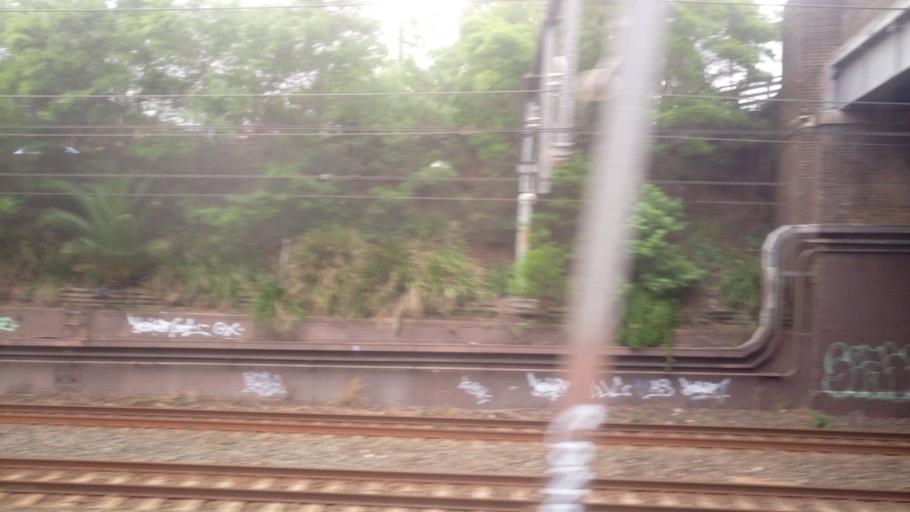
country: AU
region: New South Wales
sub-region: Marrickville
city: Lewisham
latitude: -33.8936
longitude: 151.1576
